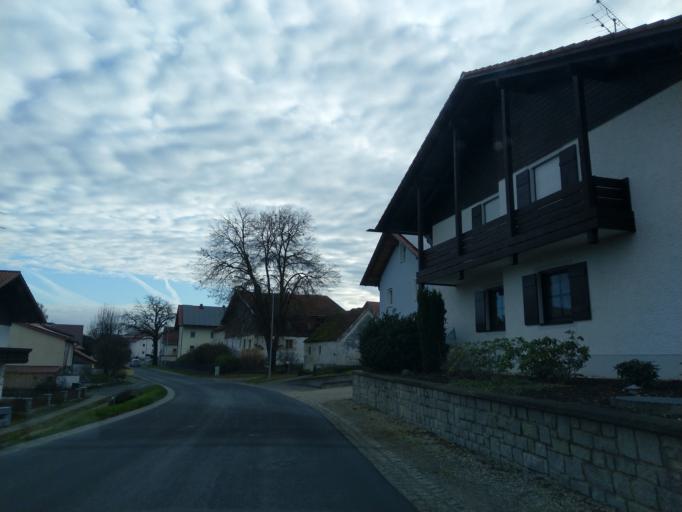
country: DE
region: Bavaria
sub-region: Lower Bavaria
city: Aholming
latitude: 48.7344
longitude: 12.9155
